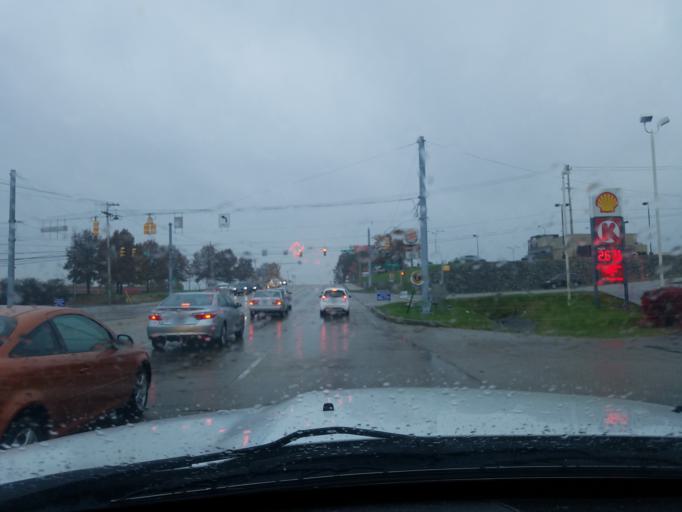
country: US
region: Indiana
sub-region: Floyd County
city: New Albany
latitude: 38.3326
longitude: -85.8185
